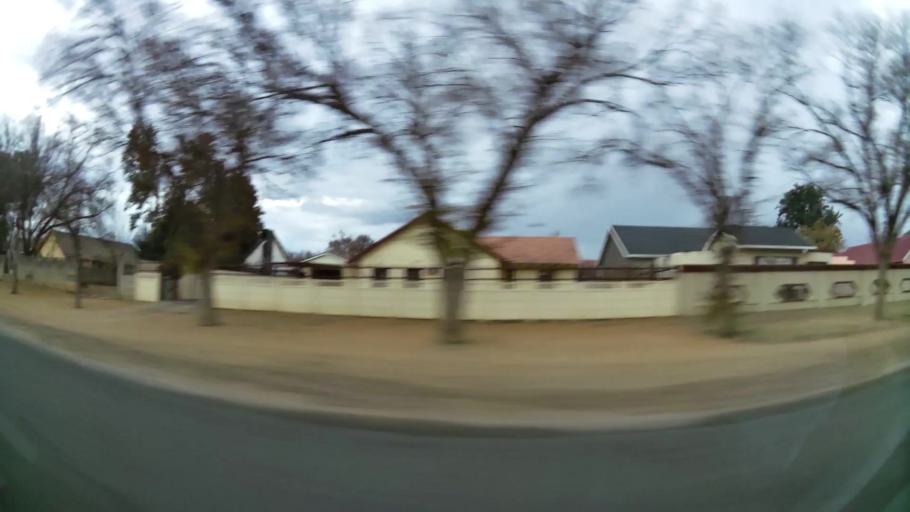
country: ZA
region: Orange Free State
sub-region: Lejweleputswa District Municipality
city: Welkom
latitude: -27.9790
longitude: 26.7580
